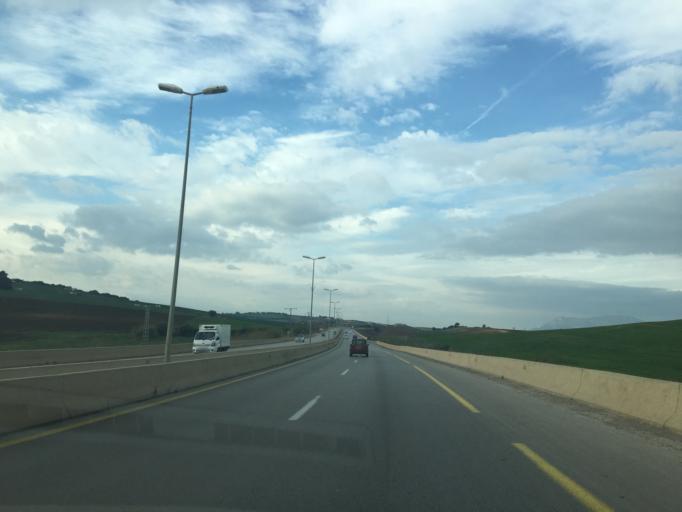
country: DZ
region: Tipaza
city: Tipasa
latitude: 36.5761
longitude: 2.5329
